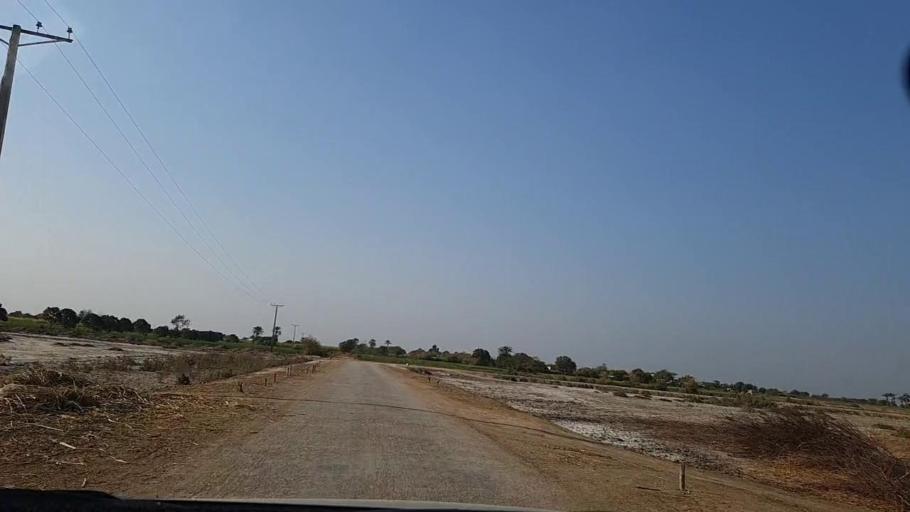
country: PK
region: Sindh
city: Mirwah Gorchani
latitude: 25.2183
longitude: 68.9917
